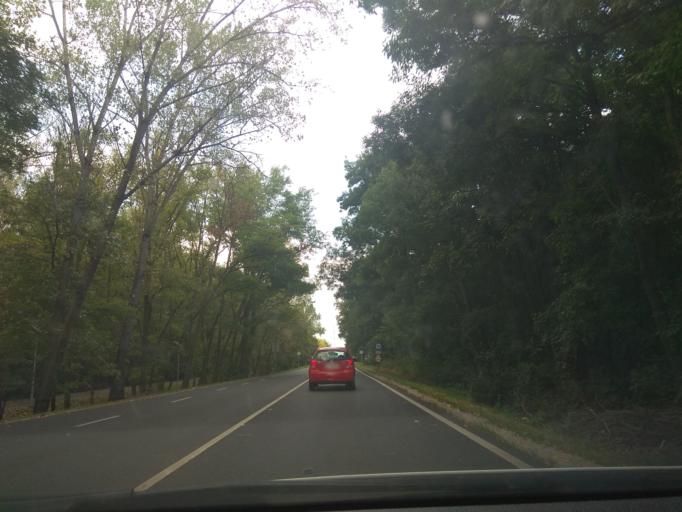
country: HU
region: Borsod-Abauj-Zemplen
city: Sajooeroes
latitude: 47.9295
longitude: 21.0273
